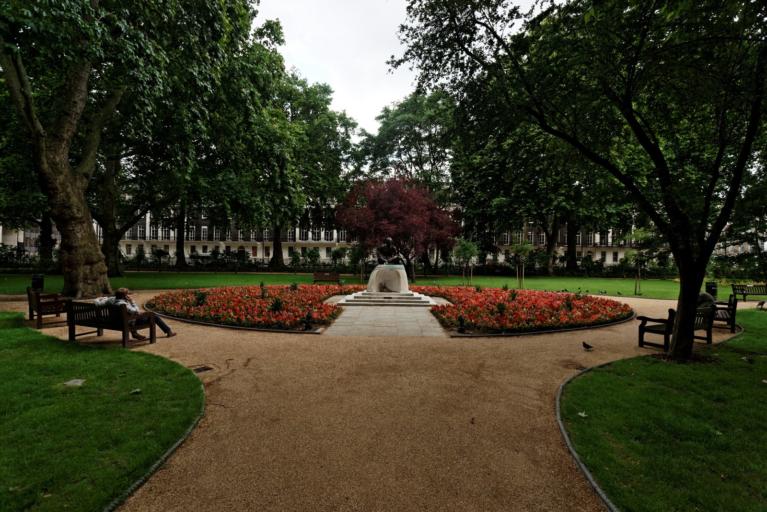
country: GB
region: England
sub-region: Greater London
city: London
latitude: 51.5251
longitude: -0.1288
